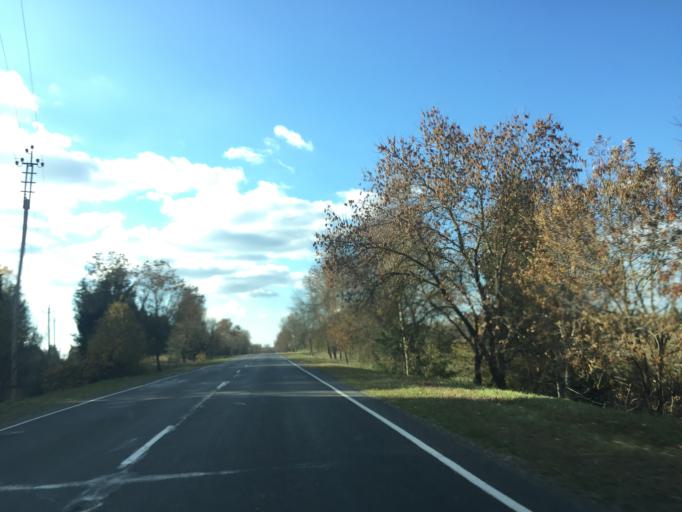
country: BY
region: Minsk
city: Narach
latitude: 54.9631
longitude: 26.6646
